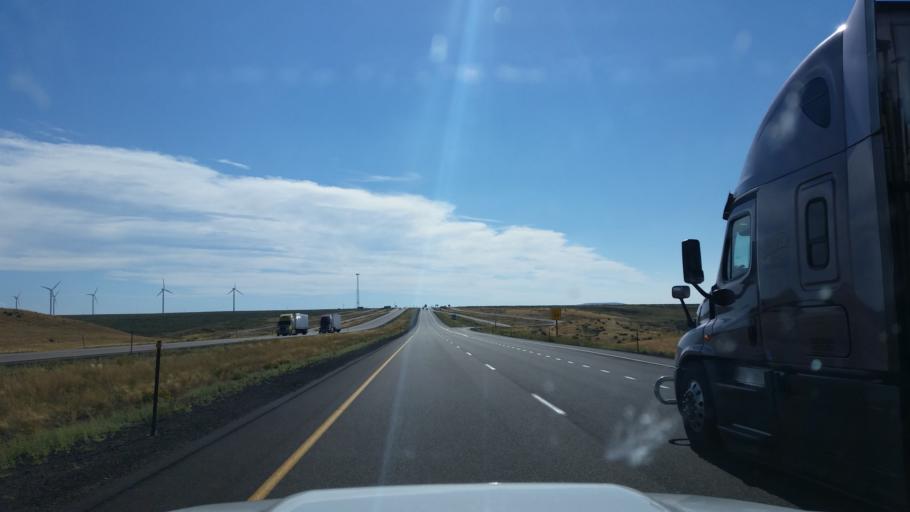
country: US
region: Wyoming
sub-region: Uinta County
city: Mountain View
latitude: 41.3047
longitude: -110.5332
